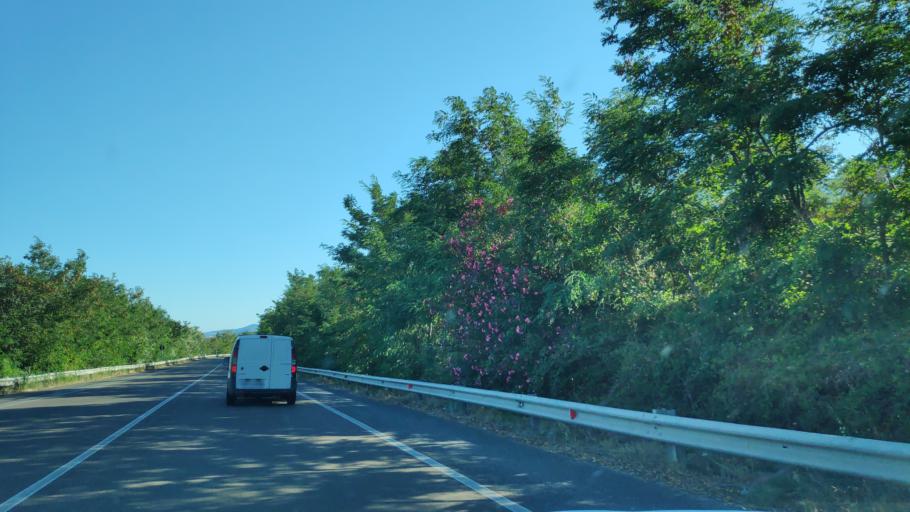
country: IT
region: Calabria
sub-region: Provincia di Catanzaro
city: Montepaone Lido
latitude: 38.7396
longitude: 16.5465
